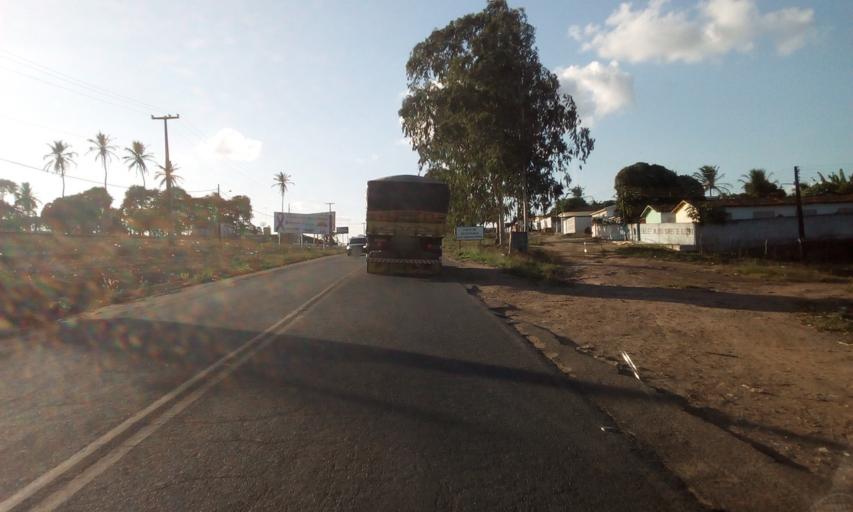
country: BR
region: Paraiba
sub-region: Mari
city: Mari
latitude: -7.0871
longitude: -35.2366
